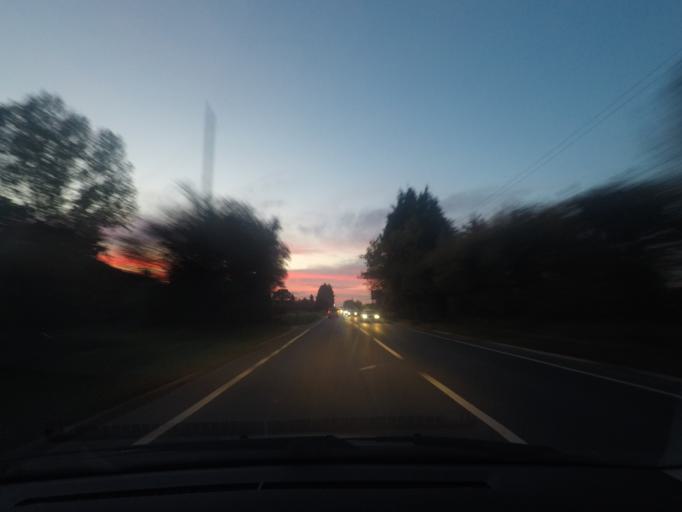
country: GB
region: England
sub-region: East Riding of Yorkshire
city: Thornton
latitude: 53.9308
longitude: -0.8278
